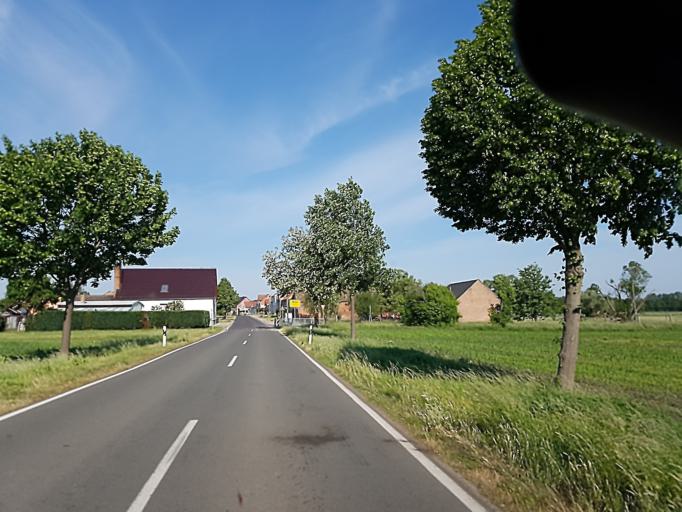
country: DE
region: Saxony-Anhalt
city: Rodleben
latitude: 52.0128
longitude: 12.2387
